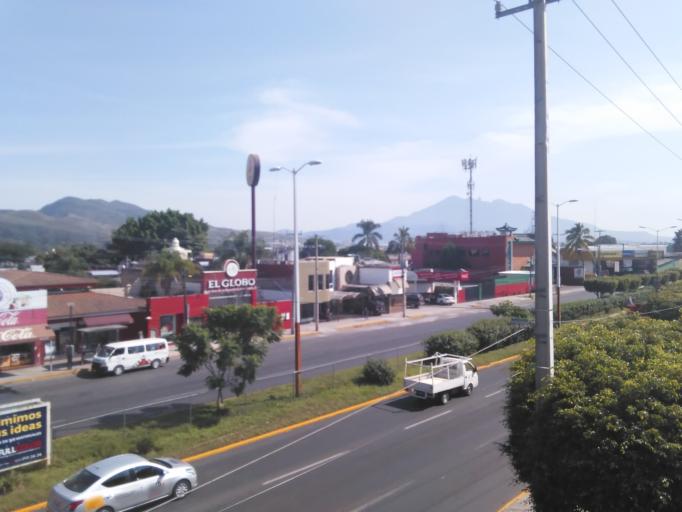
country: MX
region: Nayarit
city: Tepic
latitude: 21.4938
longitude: -104.8822
